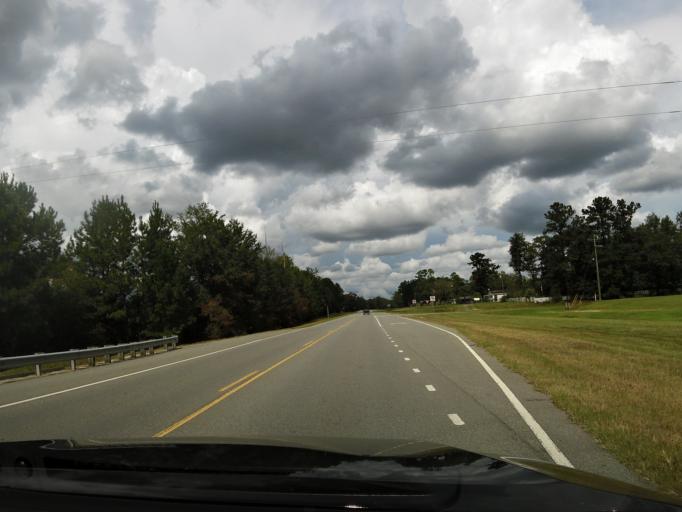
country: US
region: Georgia
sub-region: Brantley County
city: Nahunta
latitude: 31.1575
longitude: -81.9914
